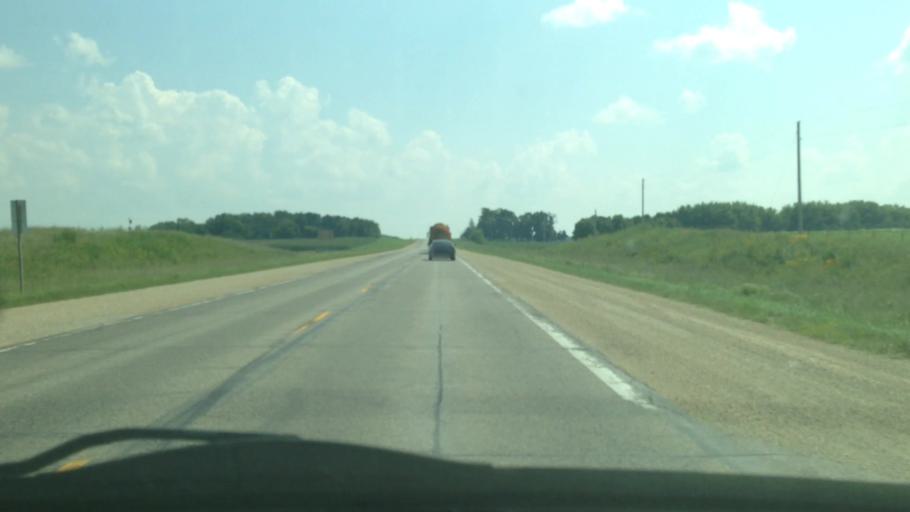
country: US
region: Iowa
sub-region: Chickasaw County
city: New Hampton
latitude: 43.2271
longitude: -92.2986
